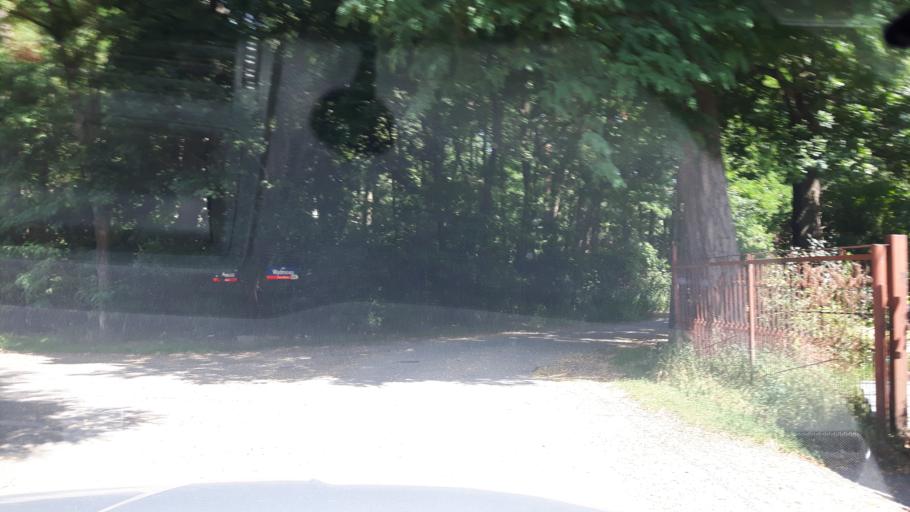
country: PL
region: Masovian Voivodeship
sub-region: Warszawa
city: Wesola
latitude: 52.2145
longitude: 21.2194
